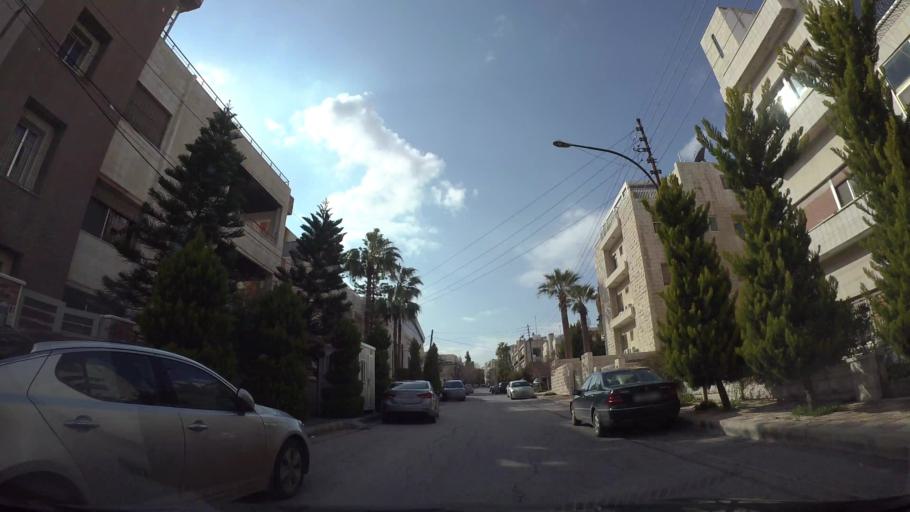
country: JO
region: Amman
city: Amman
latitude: 31.9640
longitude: 35.8946
